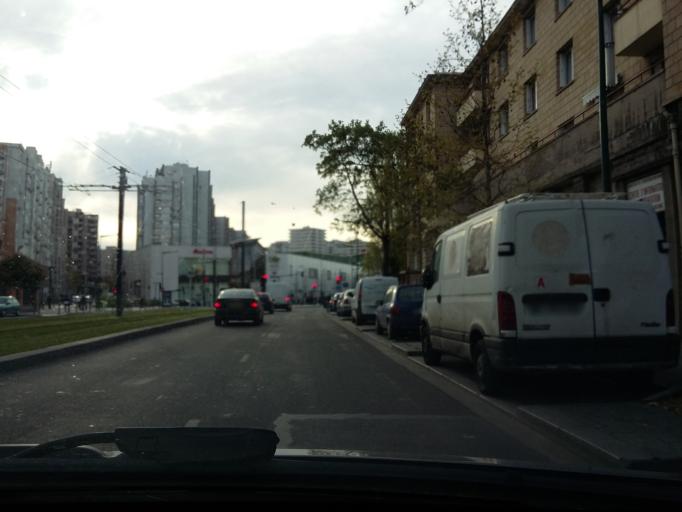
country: FR
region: Ile-de-France
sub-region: Departement de Seine-Saint-Denis
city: Epinay-sur-Seine
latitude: 48.9525
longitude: 2.3174
